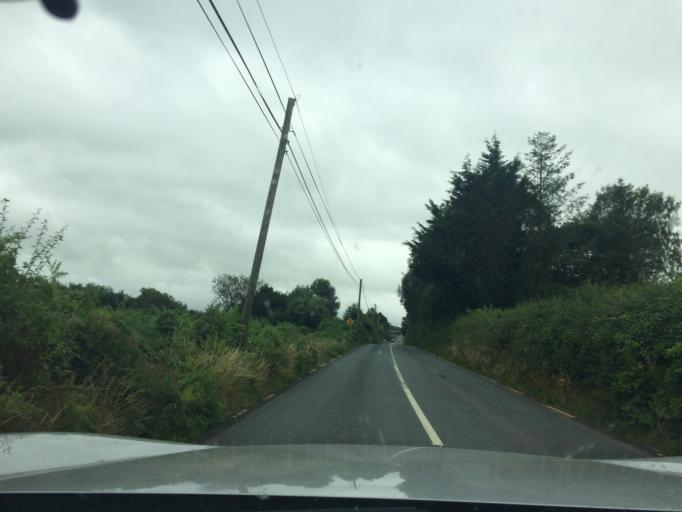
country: IE
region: Munster
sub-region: South Tipperary
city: Cluain Meala
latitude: 52.3238
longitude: -7.7608
